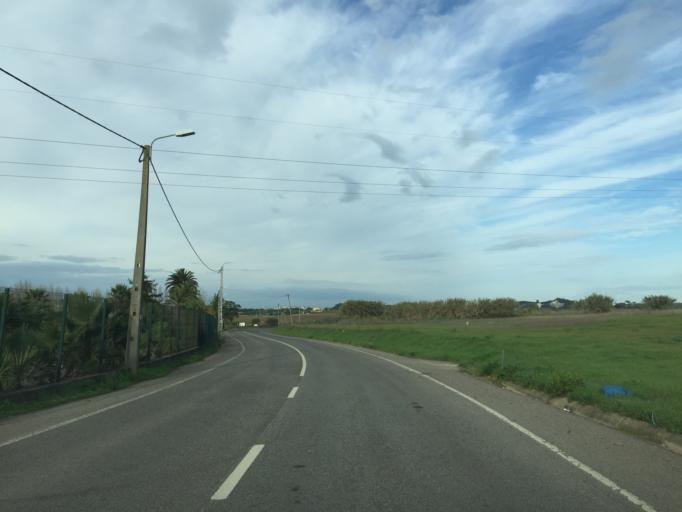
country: PT
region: Lisbon
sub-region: Sintra
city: Almargem
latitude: 38.8566
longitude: -9.2748
